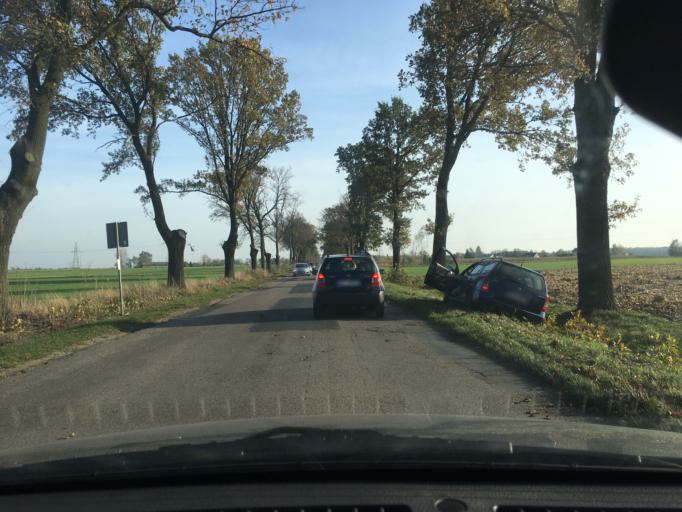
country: PL
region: Masovian Voivodeship
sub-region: Powiat plocki
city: Bodzanow
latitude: 52.4867
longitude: 20.0560
